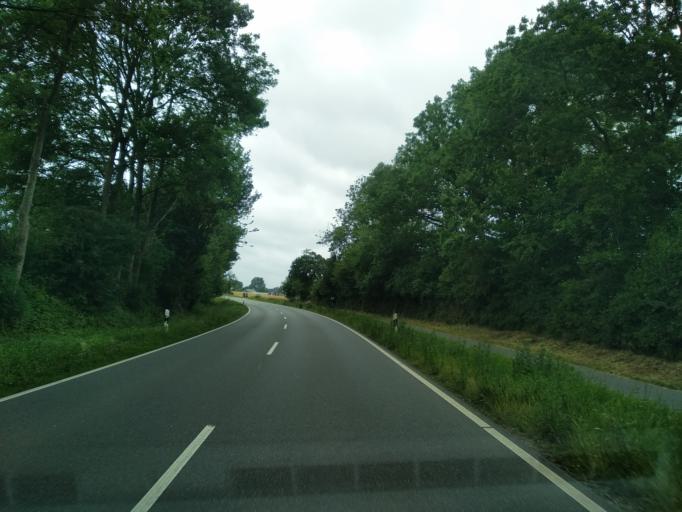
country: DE
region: Schleswig-Holstein
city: Ringsberg
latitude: 54.8038
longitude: 9.6090
